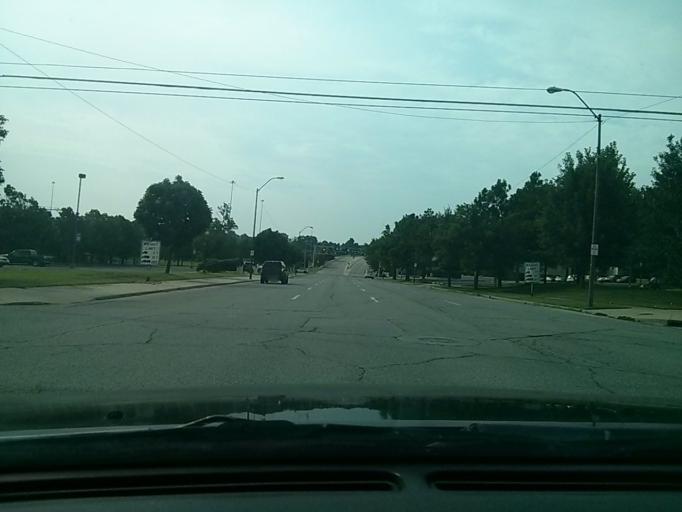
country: US
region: Oklahoma
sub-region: Tulsa County
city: Tulsa
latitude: 36.1457
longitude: -95.9842
